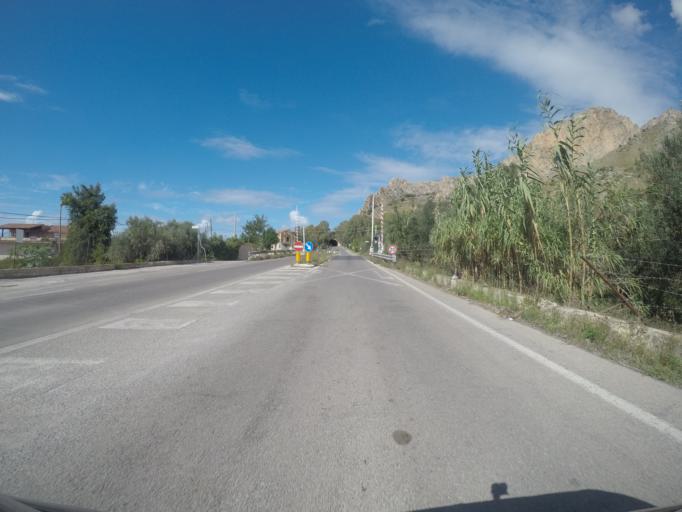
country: IT
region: Sicily
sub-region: Palermo
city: Agliandroni-Paternella
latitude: 38.1210
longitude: 13.0761
